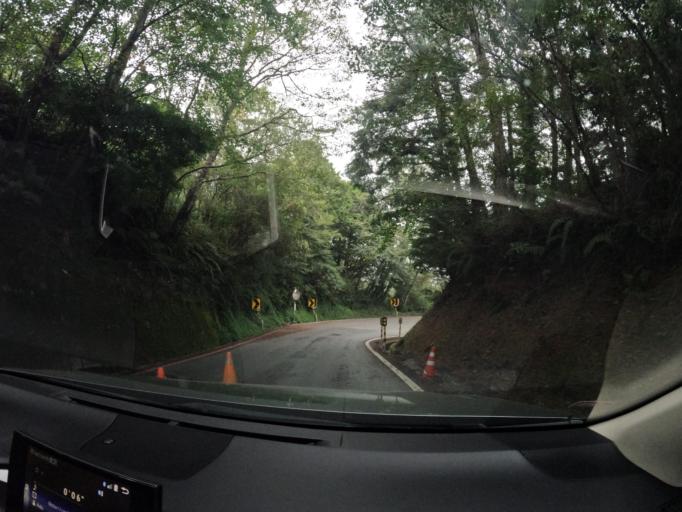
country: TW
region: Taiwan
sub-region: Taitung
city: Taitung
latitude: 23.2482
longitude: 120.9863
